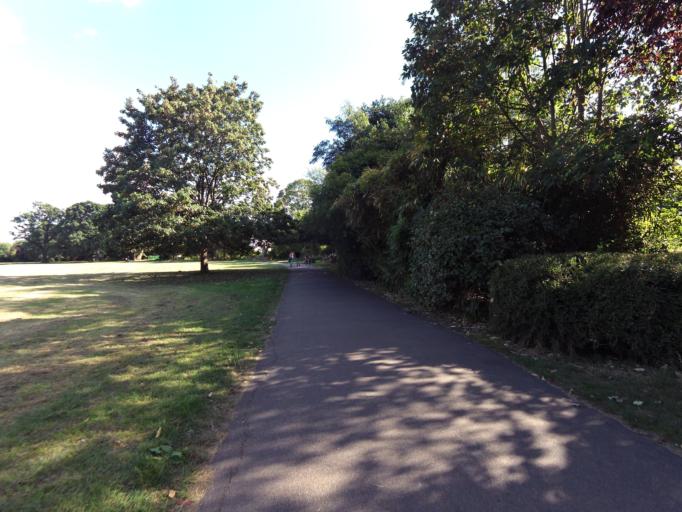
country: GB
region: England
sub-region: Greater London
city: Wood Green
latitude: 51.6188
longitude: -0.1325
